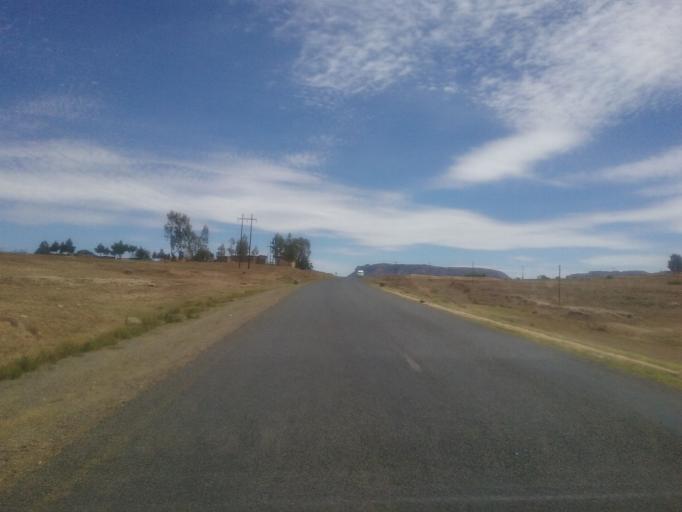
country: LS
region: Mafeteng
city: Mafeteng
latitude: -29.9832
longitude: 27.3247
